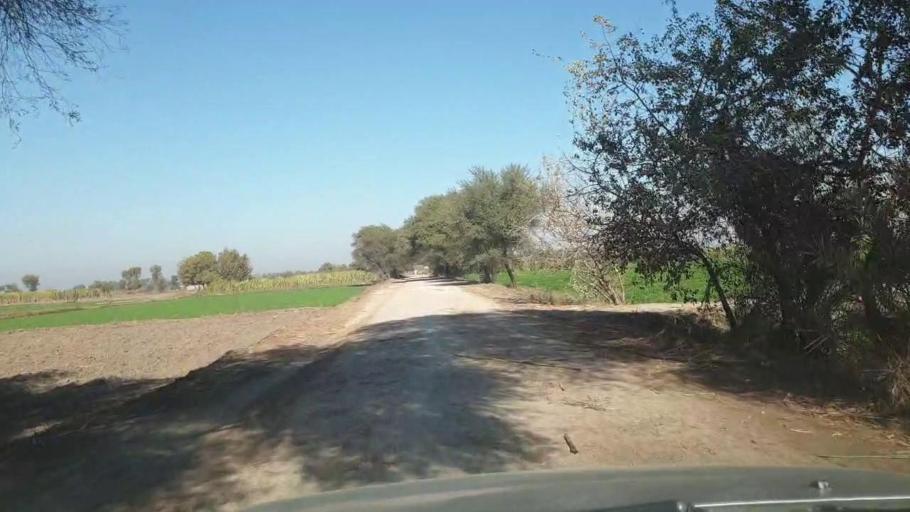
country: PK
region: Sindh
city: Ghotki
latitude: 28.0920
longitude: 69.3433
